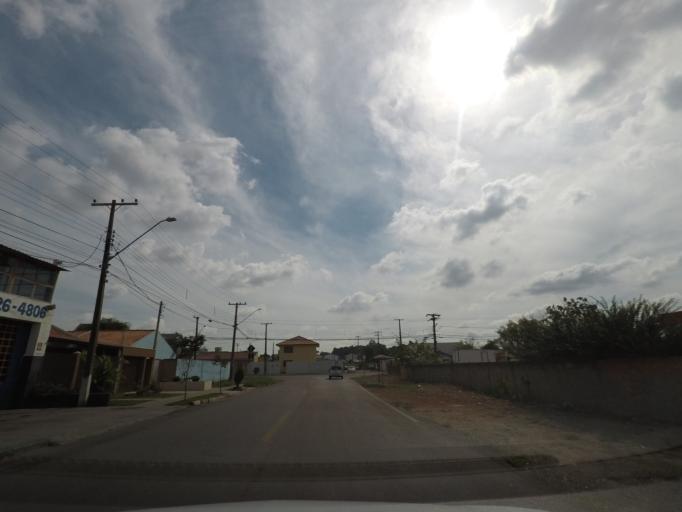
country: BR
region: Parana
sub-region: Pinhais
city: Pinhais
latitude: -25.4781
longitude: -49.1979
